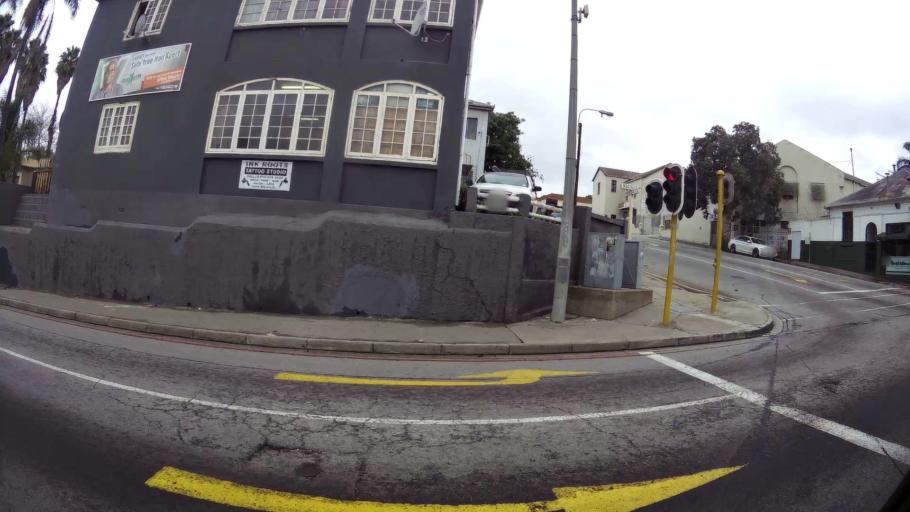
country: ZA
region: Eastern Cape
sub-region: Nelson Mandela Bay Metropolitan Municipality
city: Port Elizabeth
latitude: -33.9613
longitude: 25.6142
